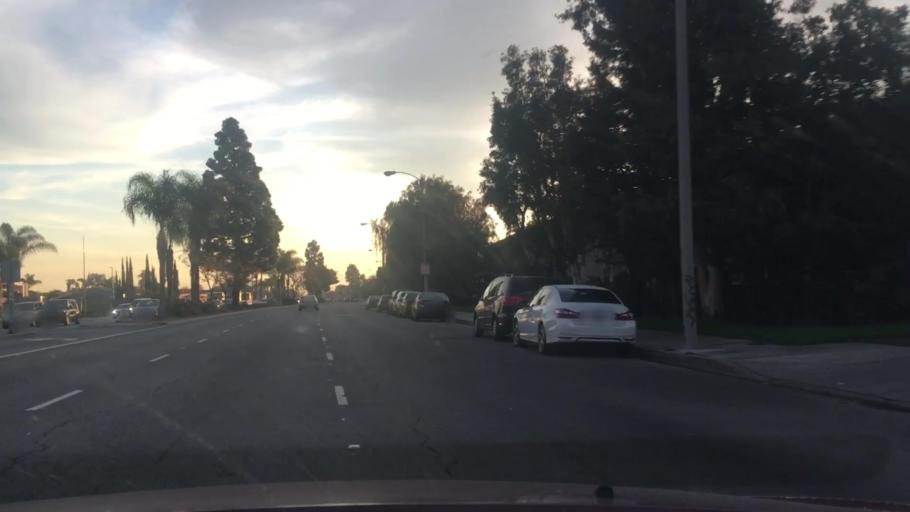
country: US
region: California
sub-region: Orange County
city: Stanton
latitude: 33.8028
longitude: -118.0090
